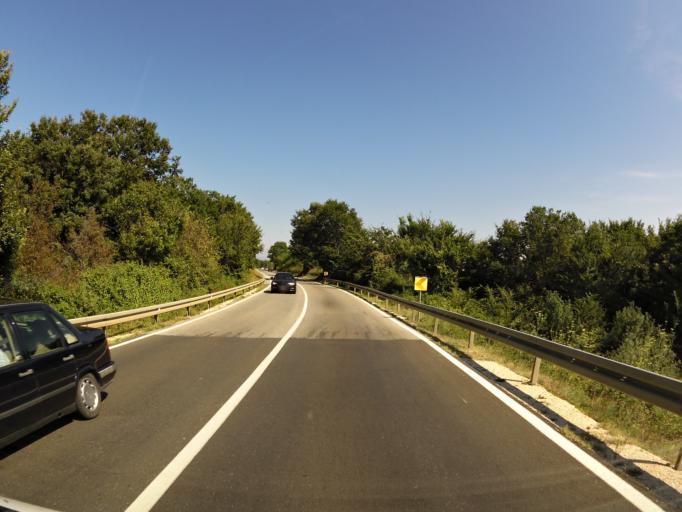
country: HR
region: Zadarska
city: Policnik
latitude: 44.1905
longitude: 15.4147
